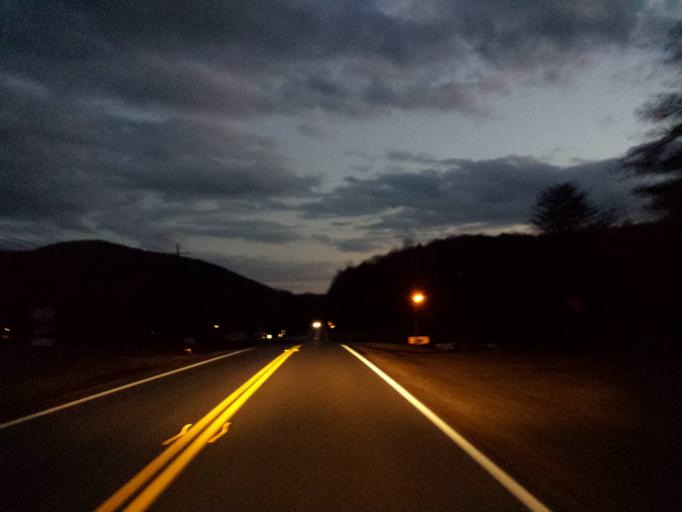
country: US
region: Georgia
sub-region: White County
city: Cleveland
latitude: 34.5734
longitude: -83.7894
